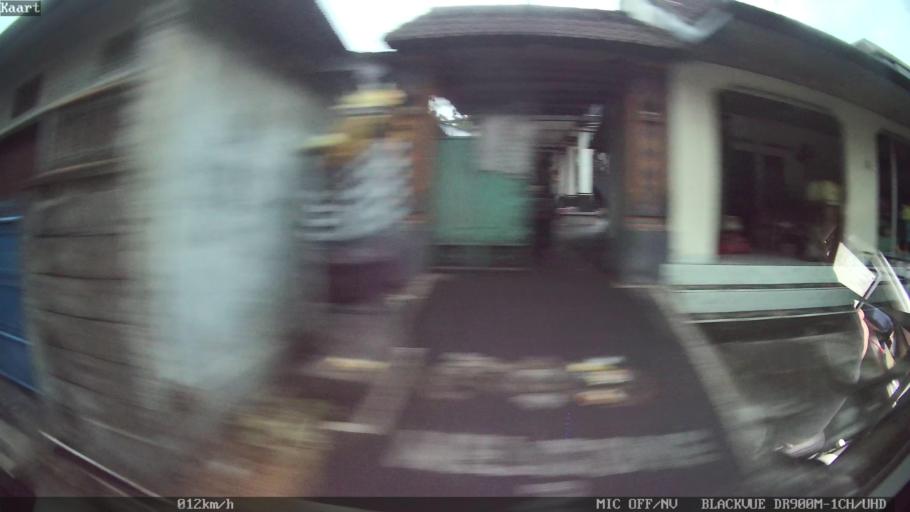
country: ID
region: Bali
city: Banjar Paangkelod
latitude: -8.6194
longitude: 115.2552
